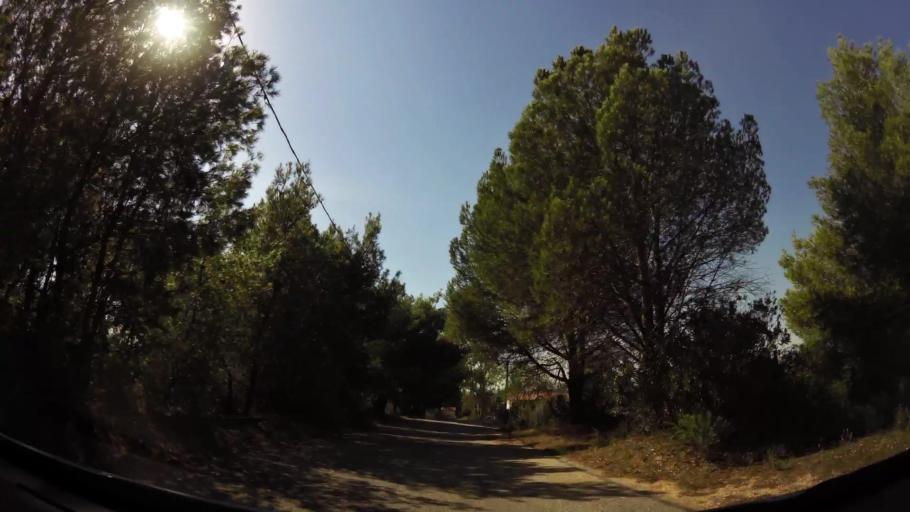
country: GR
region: Attica
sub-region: Nomarchia Athinas
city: Lykovrysi
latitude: 38.0845
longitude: 23.7739
